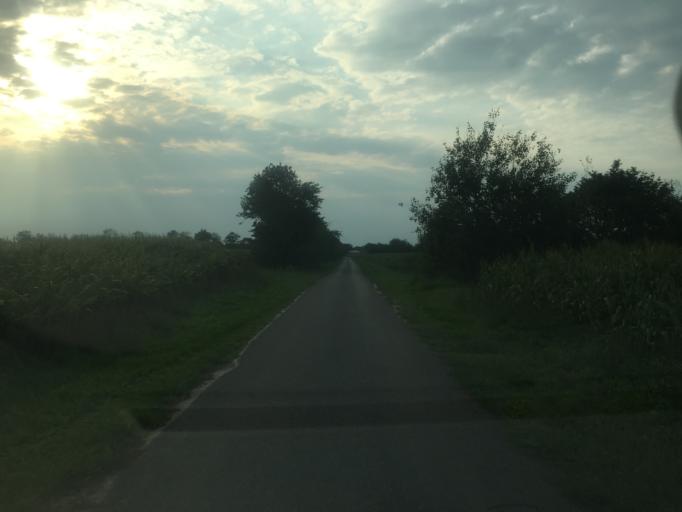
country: DK
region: South Denmark
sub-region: Tonder Kommune
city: Logumkloster
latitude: 55.0402
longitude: 8.9248
